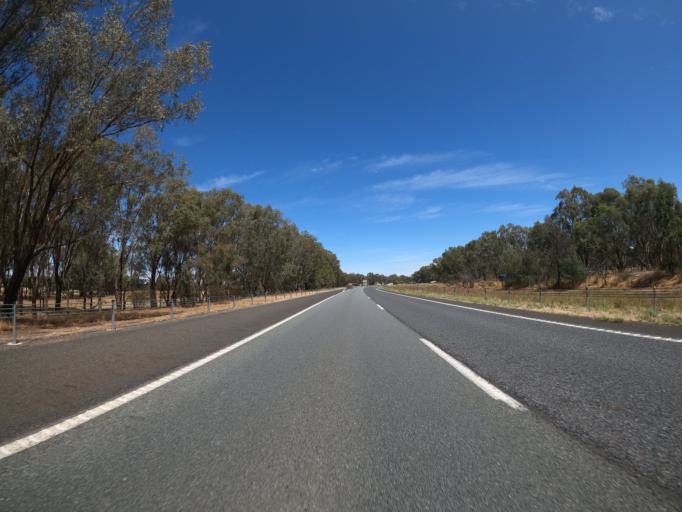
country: AU
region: Victoria
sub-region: Benalla
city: Benalla
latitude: -36.6012
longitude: 145.8698
